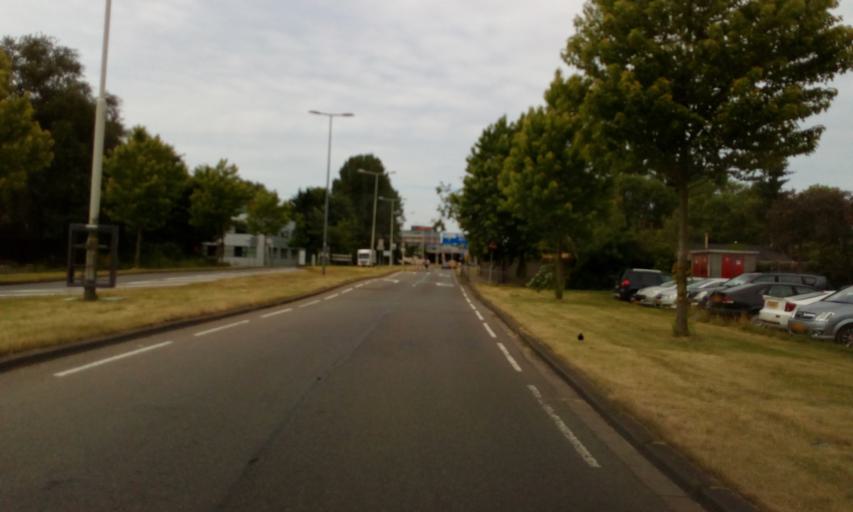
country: NL
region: South Holland
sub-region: Gemeente Rotterdam
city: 's-Gravenland
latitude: 51.9261
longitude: 4.5430
